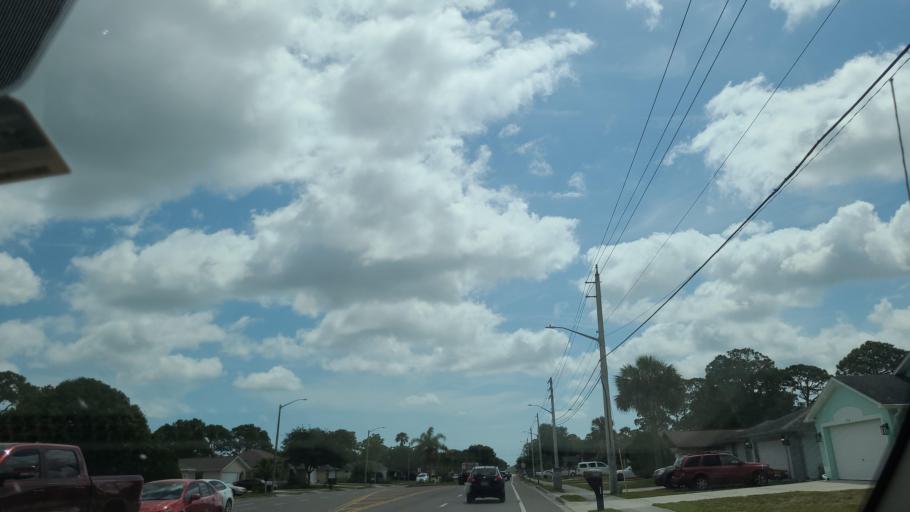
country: US
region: Florida
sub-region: Brevard County
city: June Park
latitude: 28.0318
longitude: -80.6956
